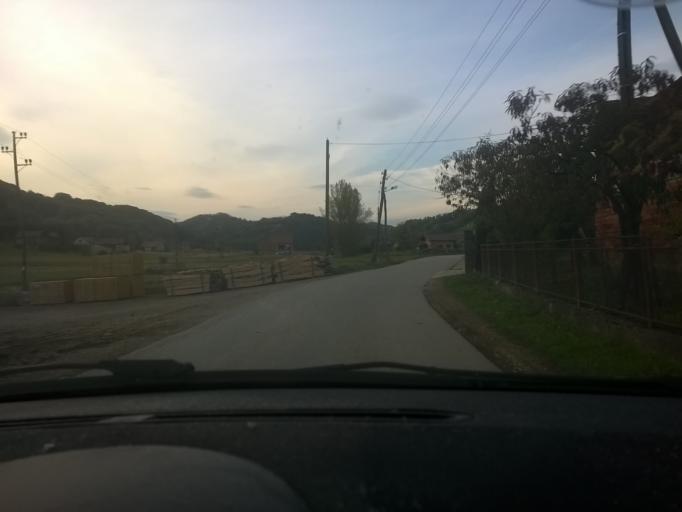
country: HR
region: Krapinsko-Zagorska
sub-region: Grad Krapina
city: Krapina
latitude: 46.0973
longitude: 15.8770
